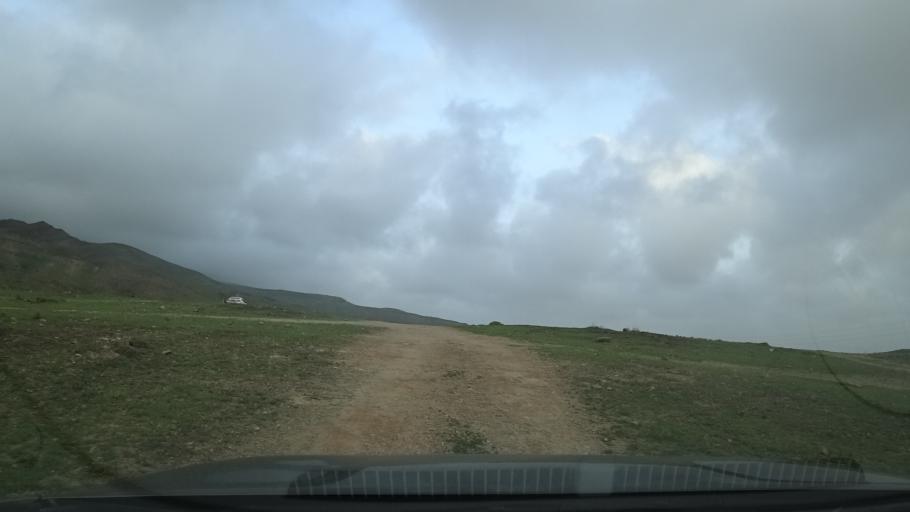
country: OM
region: Zufar
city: Salalah
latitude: 17.1181
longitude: 54.2297
